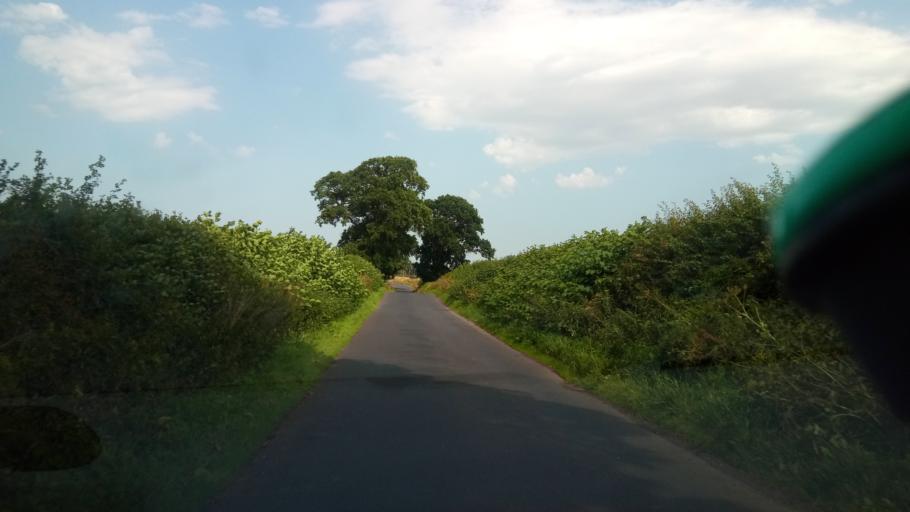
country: GB
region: Scotland
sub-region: The Scottish Borders
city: Kelso
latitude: 55.5849
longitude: -2.4724
